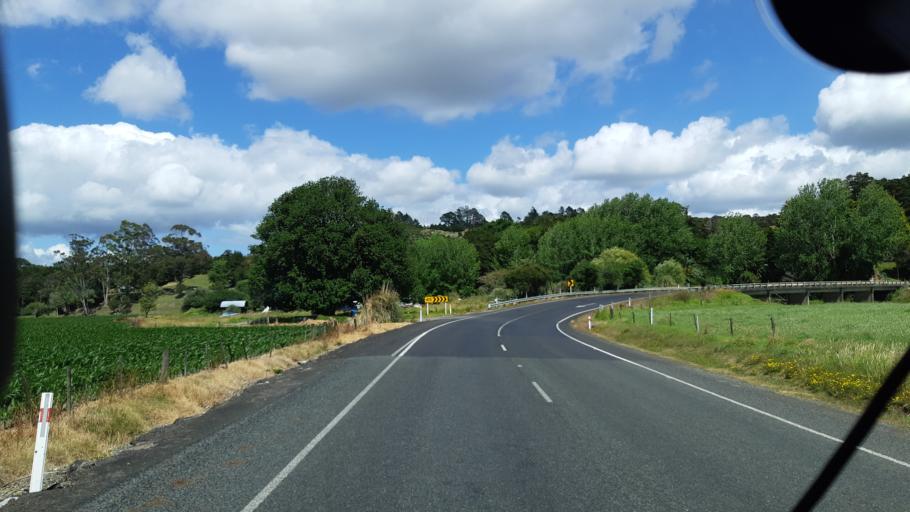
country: NZ
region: Northland
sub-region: Far North District
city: Waimate North
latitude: -35.3068
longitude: 173.6433
